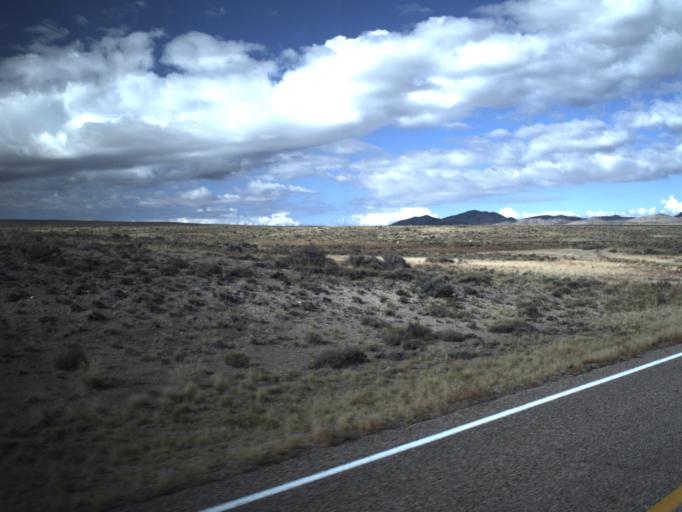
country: US
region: Utah
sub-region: Beaver County
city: Milford
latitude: 38.4341
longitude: -113.1351
